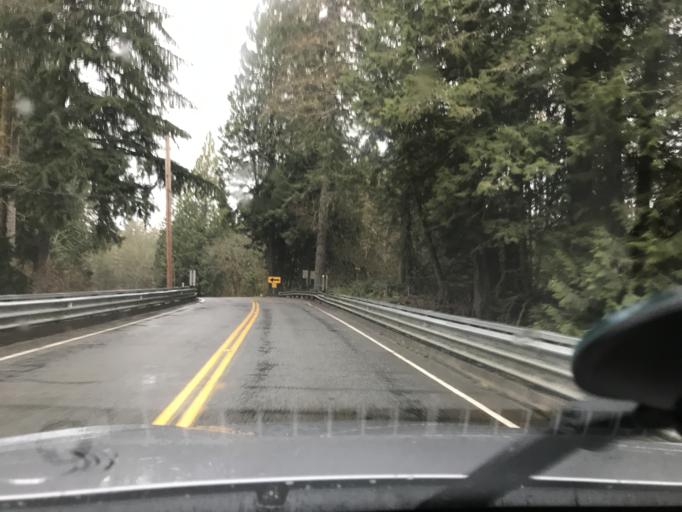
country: US
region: Washington
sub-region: King County
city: Ames Lake
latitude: 47.6591
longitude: -121.9656
